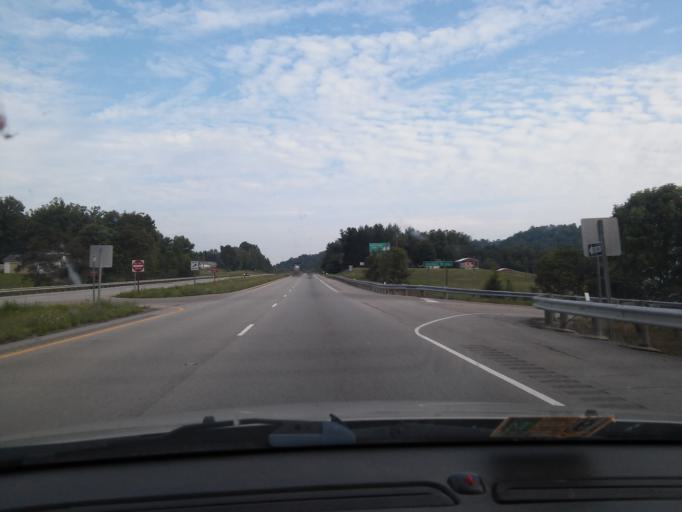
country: US
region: Ohio
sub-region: Jackson County
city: Jackson
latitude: 39.1728
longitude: -82.7465
